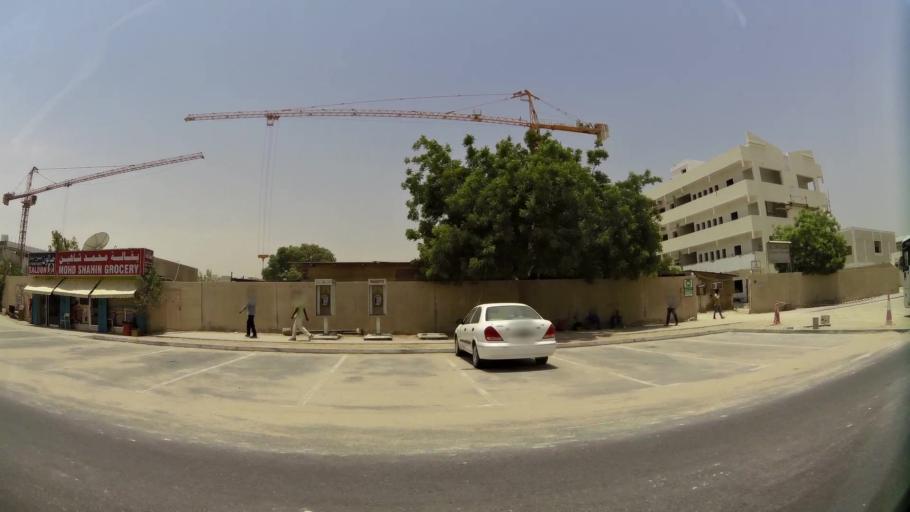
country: AE
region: Ash Shariqah
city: Sharjah
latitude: 25.2648
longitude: 55.4272
